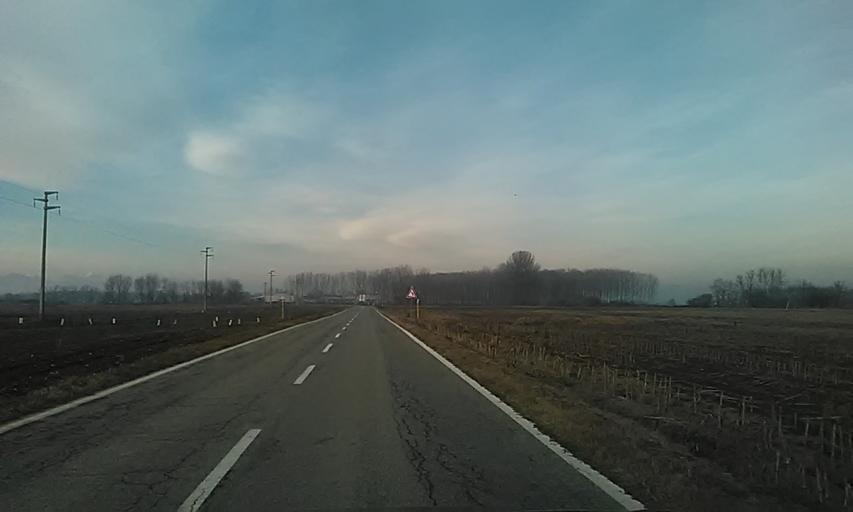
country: IT
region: Piedmont
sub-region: Provincia di Novara
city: Recetto
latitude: 45.4699
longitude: 8.4302
